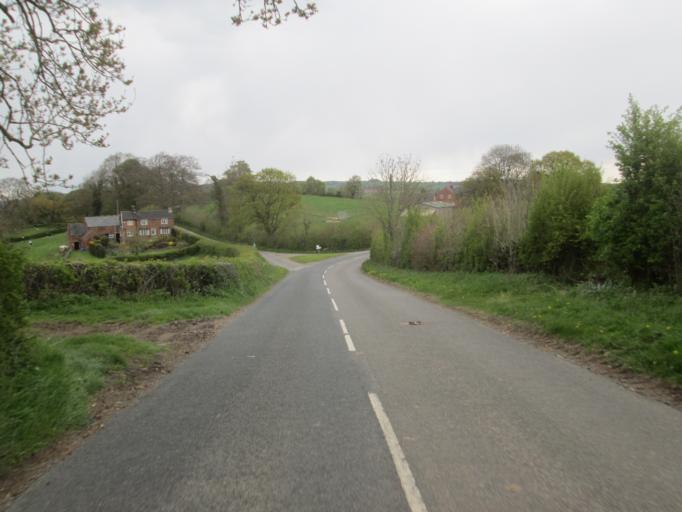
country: GB
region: England
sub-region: Derbyshire
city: Wirksworth
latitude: 53.0171
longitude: -1.5772
